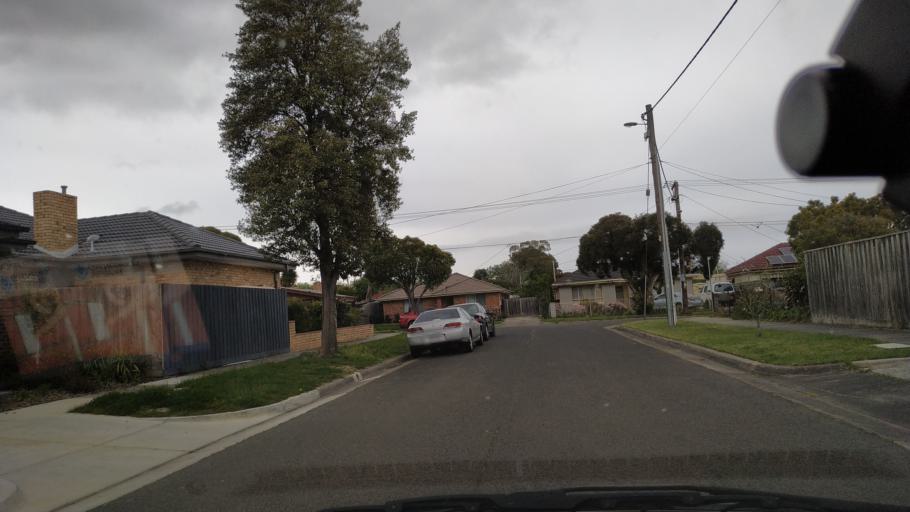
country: AU
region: Victoria
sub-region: Greater Dandenong
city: Dandenong North
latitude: -37.9657
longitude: 145.2018
